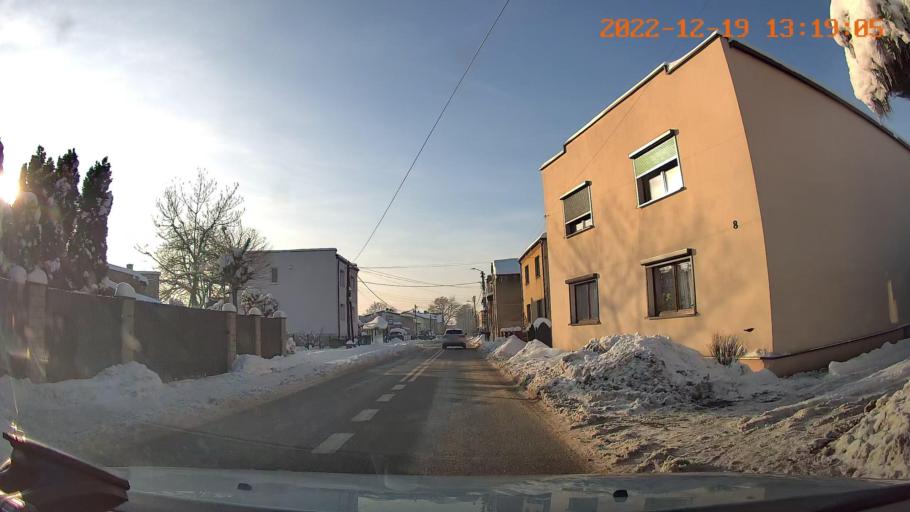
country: PL
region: Silesian Voivodeship
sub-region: Powiat bierunsko-ledzinski
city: Chelm Slaski
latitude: 50.1075
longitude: 19.1945
